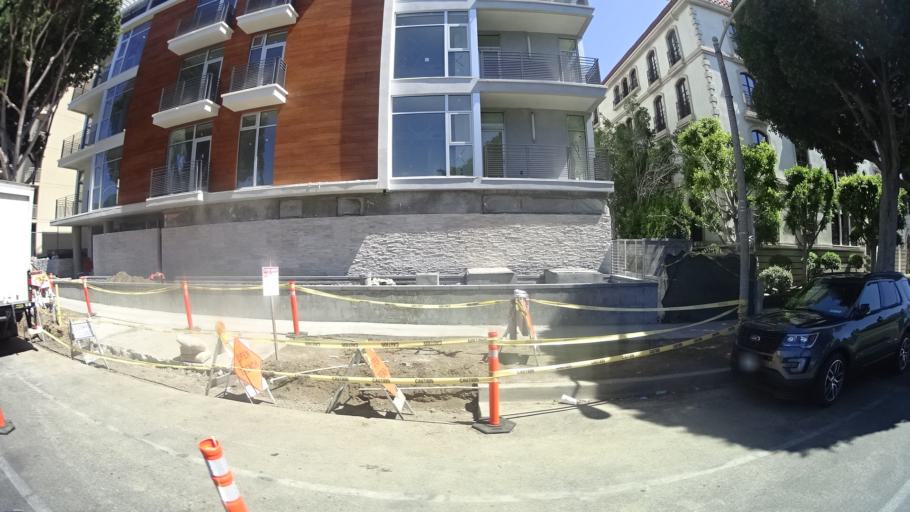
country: US
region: California
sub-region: Los Angeles County
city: Beverly Hills
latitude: 34.0723
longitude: -118.3946
